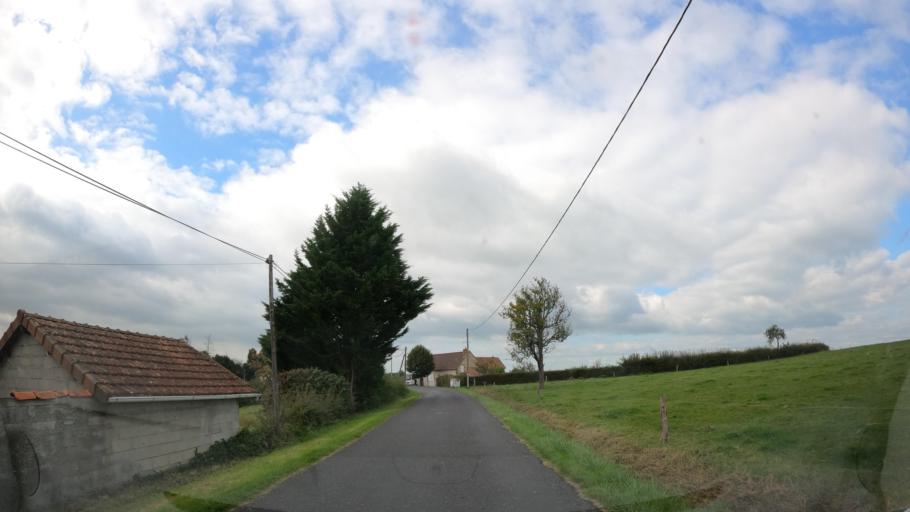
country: FR
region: Auvergne
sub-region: Departement de l'Allier
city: Lapalisse
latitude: 46.3431
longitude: 3.6401
